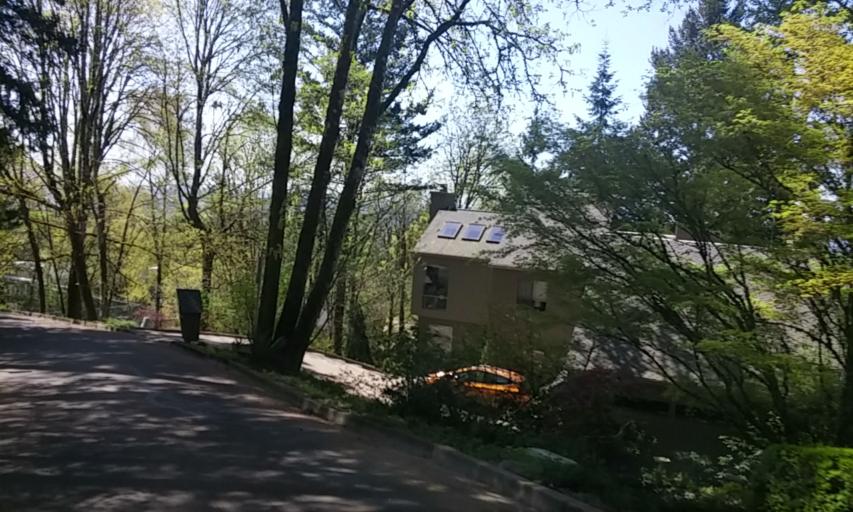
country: US
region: Oregon
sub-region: Washington County
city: West Haven-Sylvan
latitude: 45.5177
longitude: -122.7636
